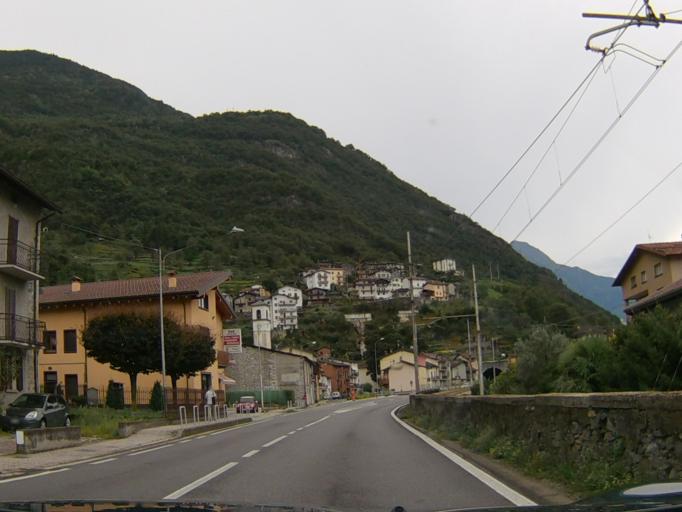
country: IT
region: Lombardy
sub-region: Provincia di Sondrio
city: Verceia
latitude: 46.1970
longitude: 9.4514
